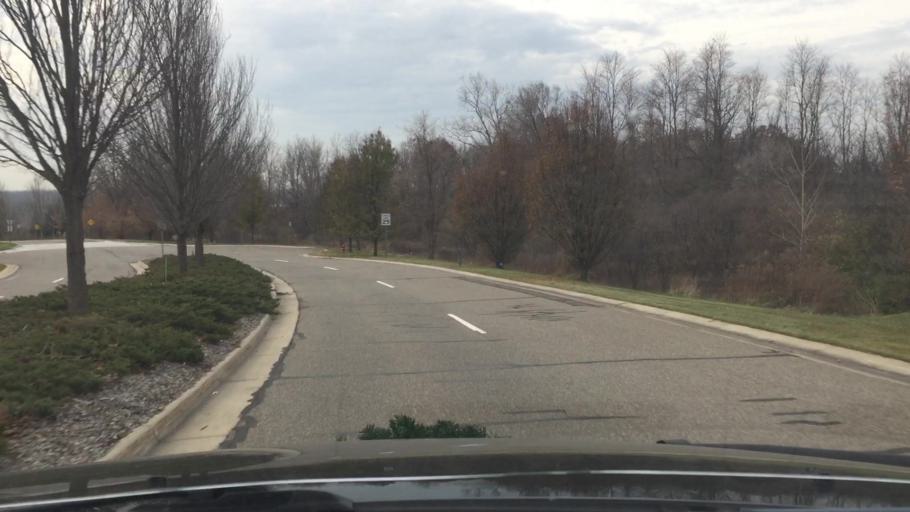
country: US
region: Michigan
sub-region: Oakland County
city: Auburn Hills
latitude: 42.6986
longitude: -83.2553
